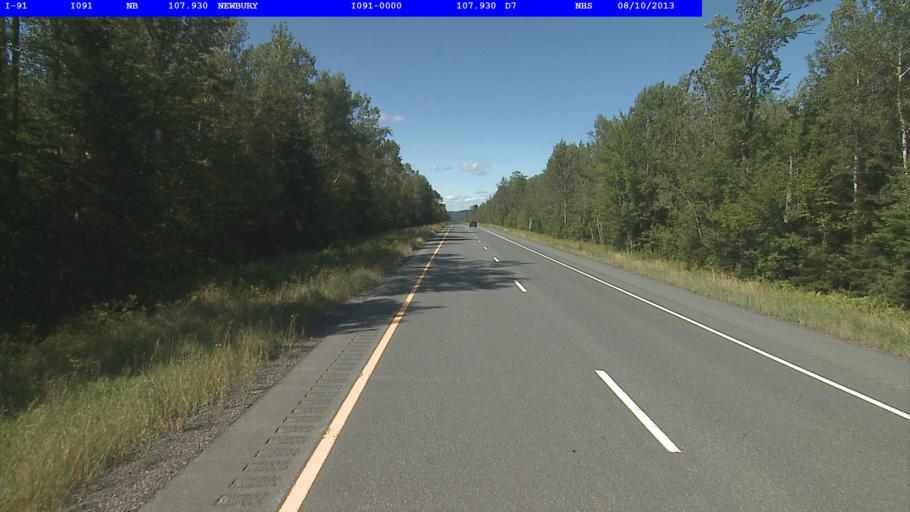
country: US
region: New Hampshire
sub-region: Grafton County
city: Woodsville
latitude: 44.1274
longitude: -72.1036
